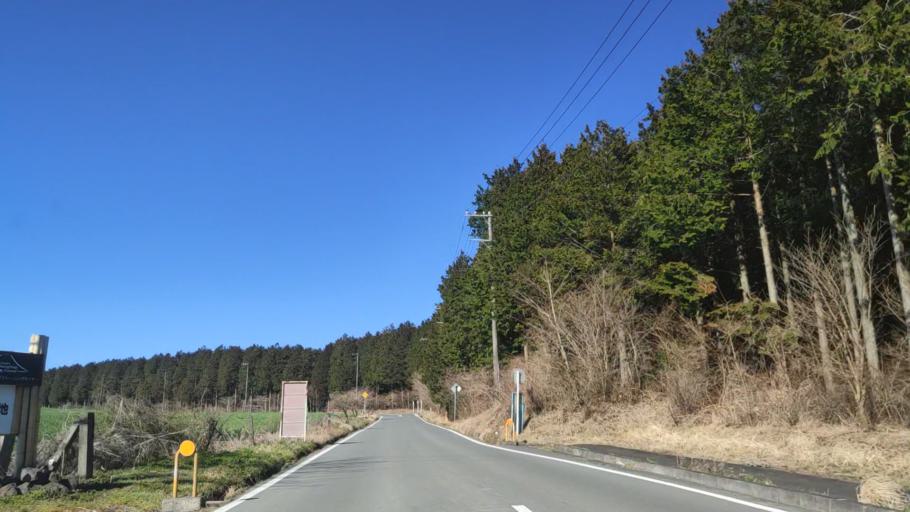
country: JP
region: Yamanashi
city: Fujikawaguchiko
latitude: 35.3771
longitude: 138.6045
